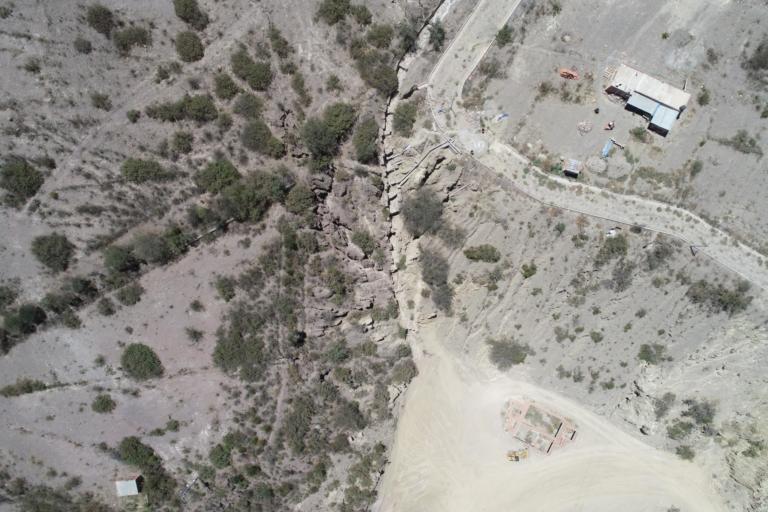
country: BO
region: La Paz
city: La Paz
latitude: -16.6158
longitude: -68.0602
